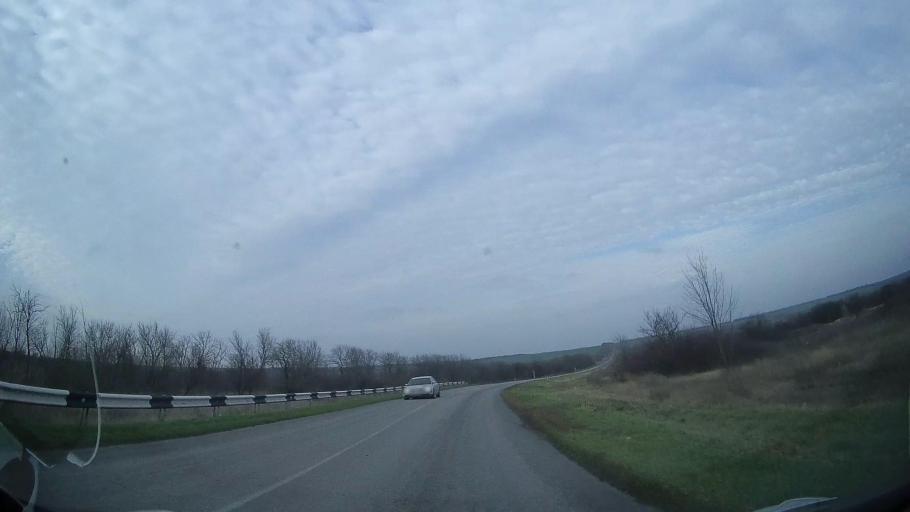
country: RU
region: Rostov
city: Zernograd
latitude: 46.8887
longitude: 40.3393
